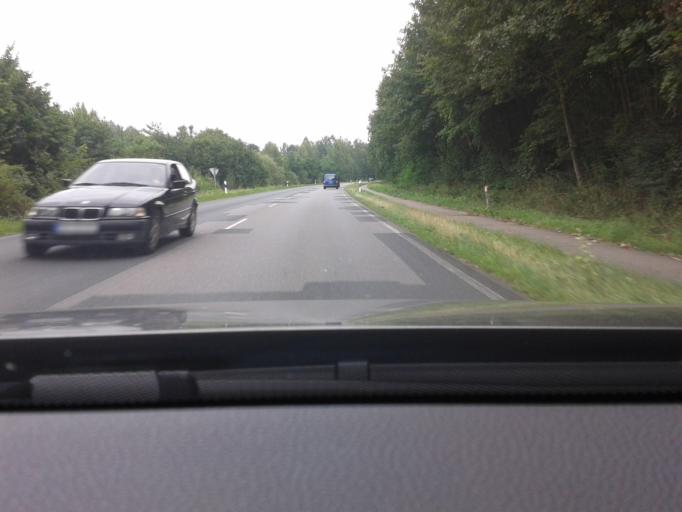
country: DE
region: Lower Saxony
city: Gifhorn
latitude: 52.4890
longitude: 10.5719
